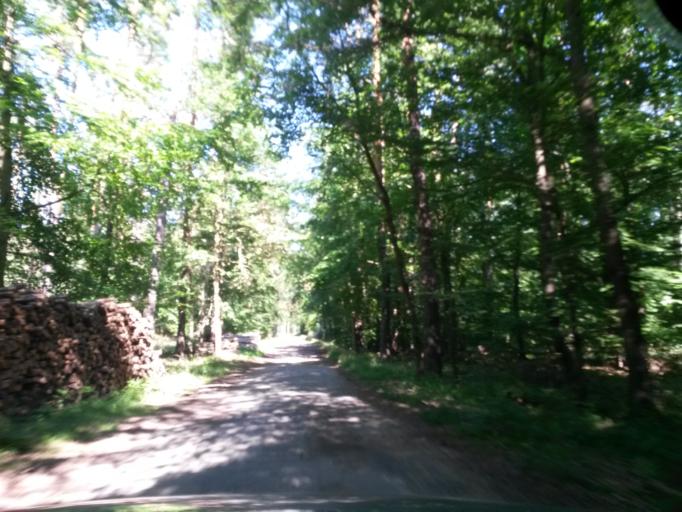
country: DE
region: Brandenburg
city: Templin
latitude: 53.2045
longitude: 13.4545
